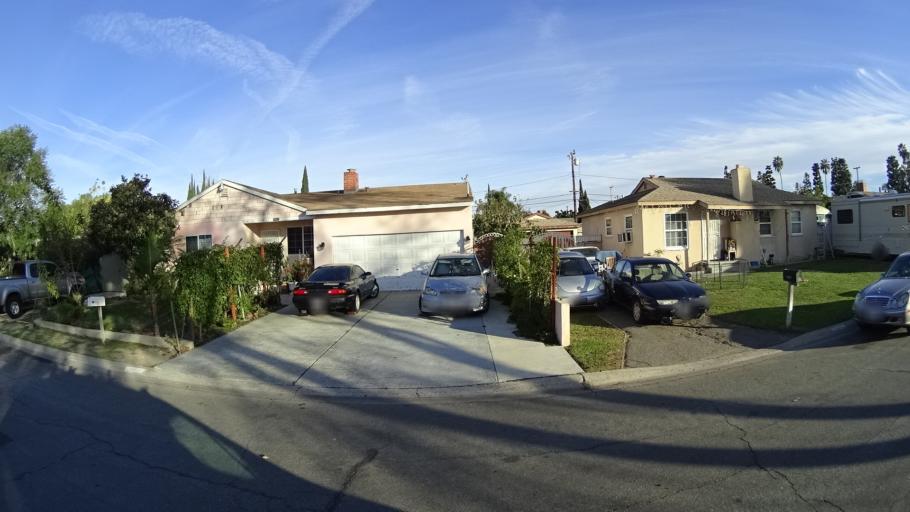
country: US
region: California
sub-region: Orange County
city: Garden Grove
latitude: 33.7710
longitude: -117.9474
